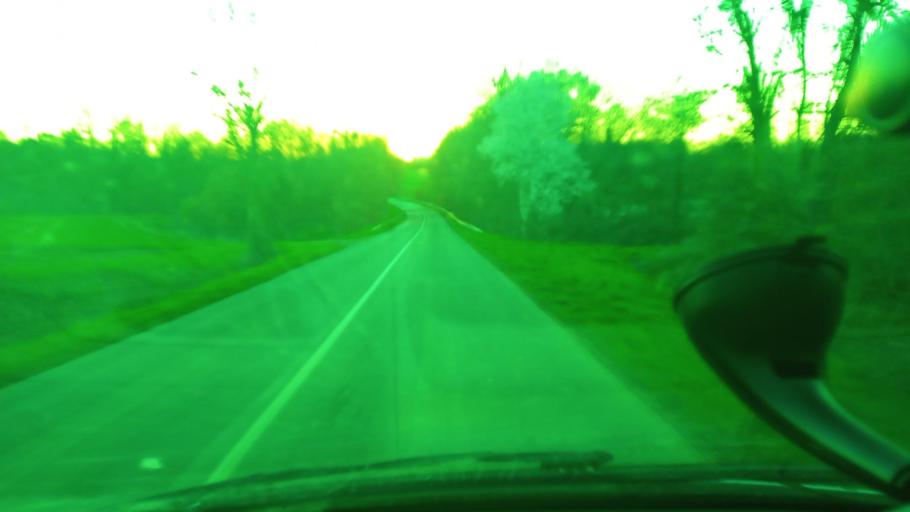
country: FR
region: Pays de la Loire
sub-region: Departement de la Vendee
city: Saligny
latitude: 46.7967
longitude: -1.4061
